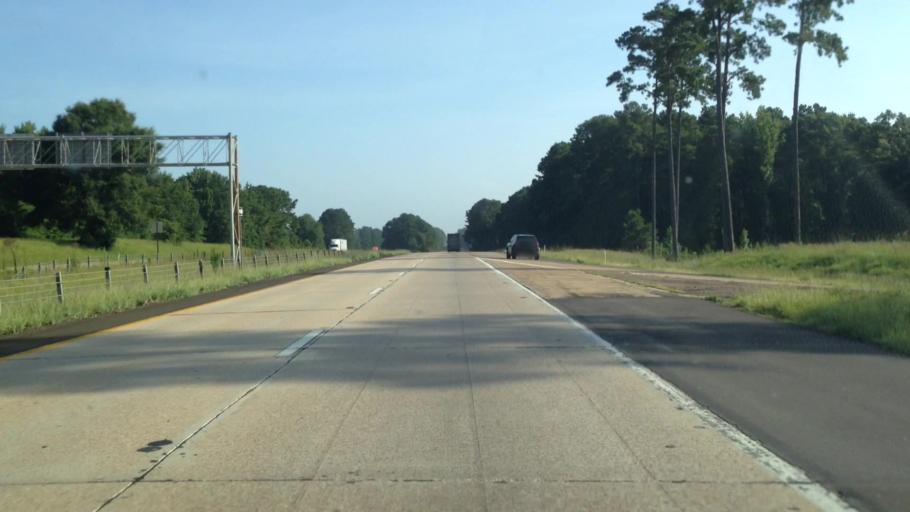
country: US
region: Mississippi
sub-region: Pike County
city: Summit
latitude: 31.2910
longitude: -90.4784
